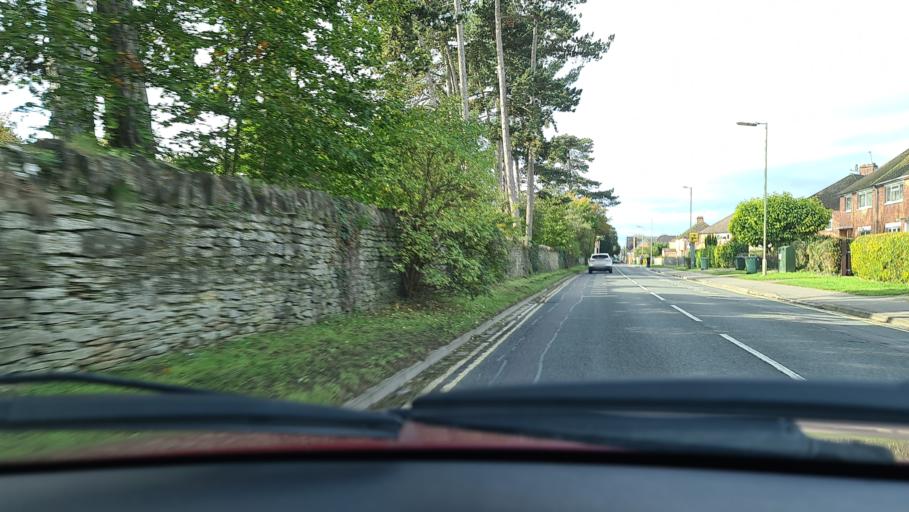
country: GB
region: England
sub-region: Oxfordshire
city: Bicester
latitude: 51.8974
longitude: -1.1444
